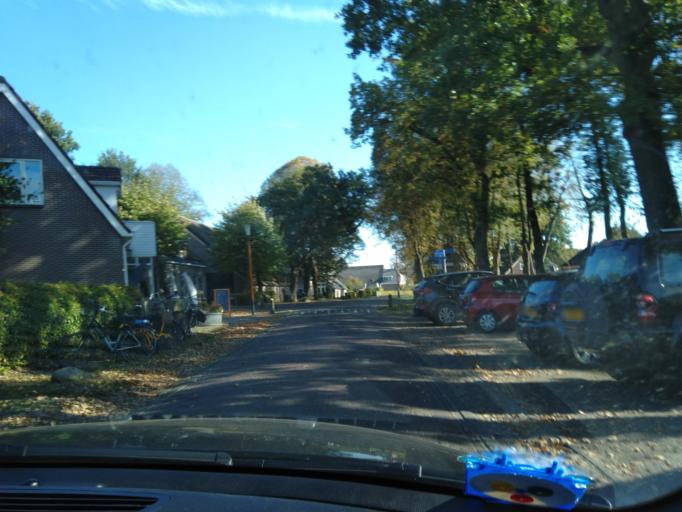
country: NL
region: Drenthe
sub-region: Gemeente Assen
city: Assen
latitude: 53.0130
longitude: 6.6114
